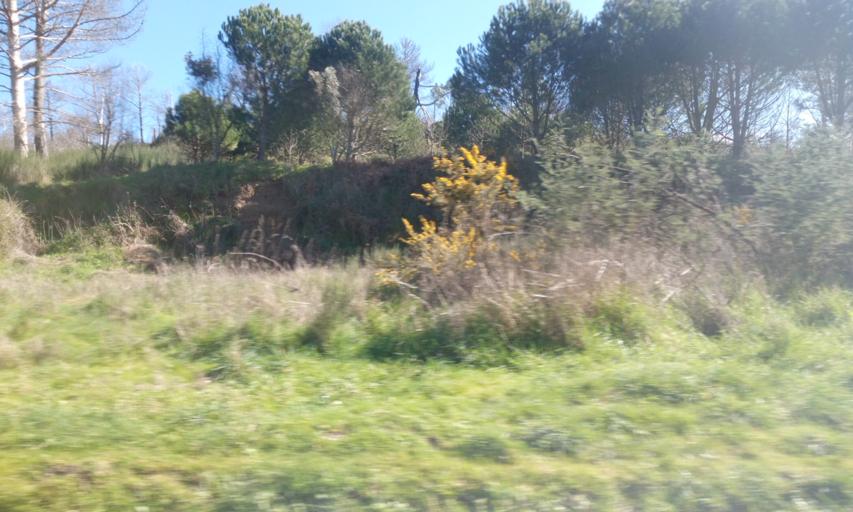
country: PT
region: Guarda
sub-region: Manteigas
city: Manteigas
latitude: 40.4781
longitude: -7.6173
